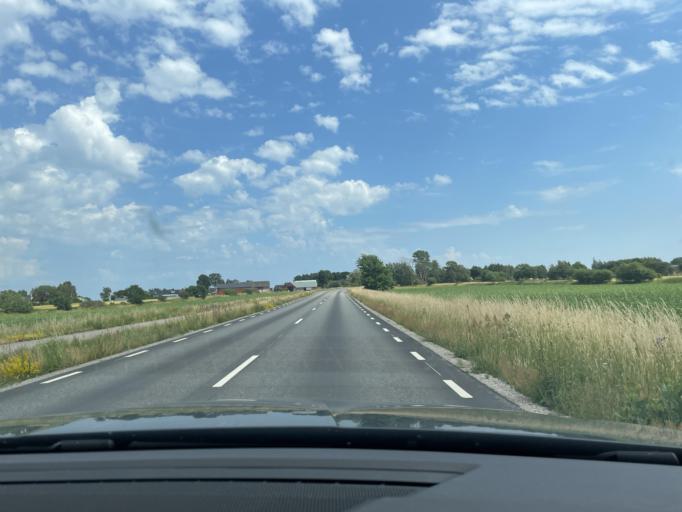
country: SE
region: Blekinge
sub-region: Solvesborgs Kommun
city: Soelvesborg
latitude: 56.0427
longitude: 14.6819
